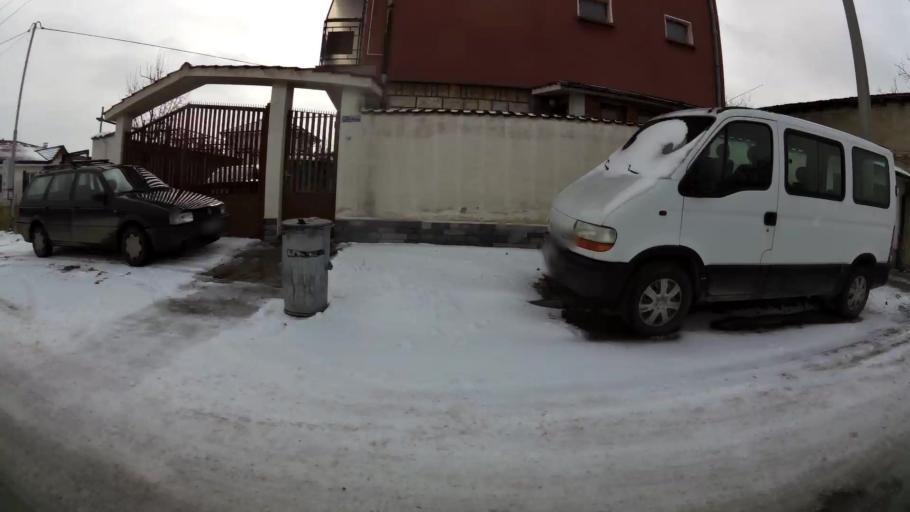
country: BG
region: Sofia-Capital
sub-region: Stolichna Obshtina
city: Sofia
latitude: 42.7169
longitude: 23.4077
